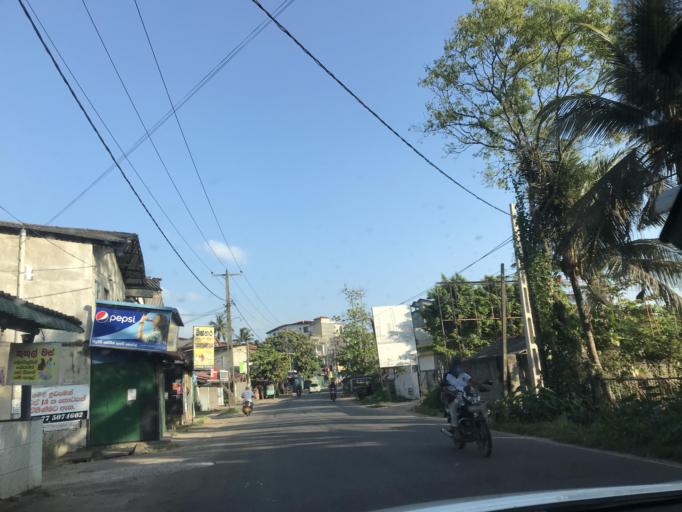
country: LK
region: Western
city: Ja Ela
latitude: 7.0864
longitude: 79.8922
